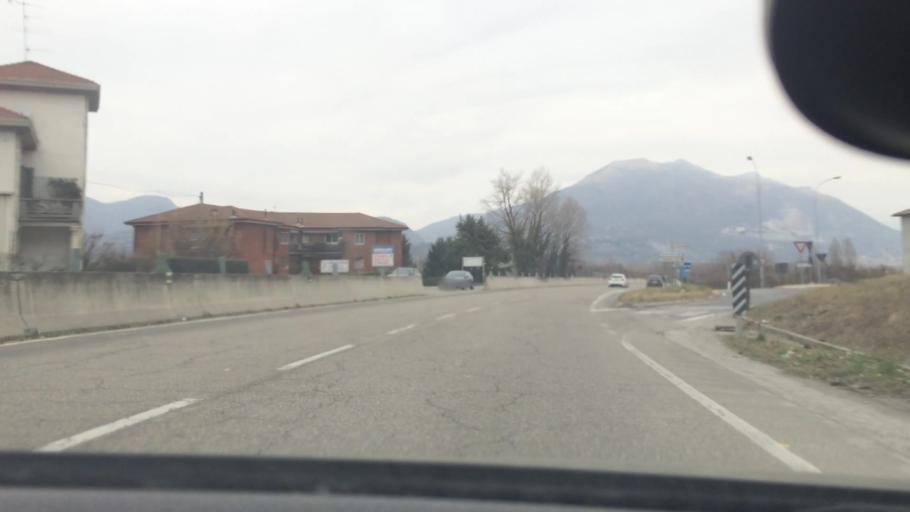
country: IT
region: Lombardy
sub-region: Provincia di Como
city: Merone
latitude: 45.7841
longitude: 9.2392
